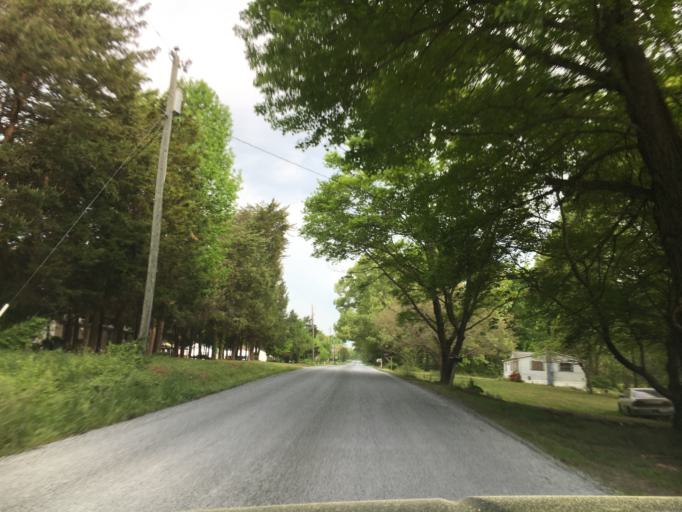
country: US
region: Virginia
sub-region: Campbell County
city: Brookneal
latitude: 36.9525
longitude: -78.9687
